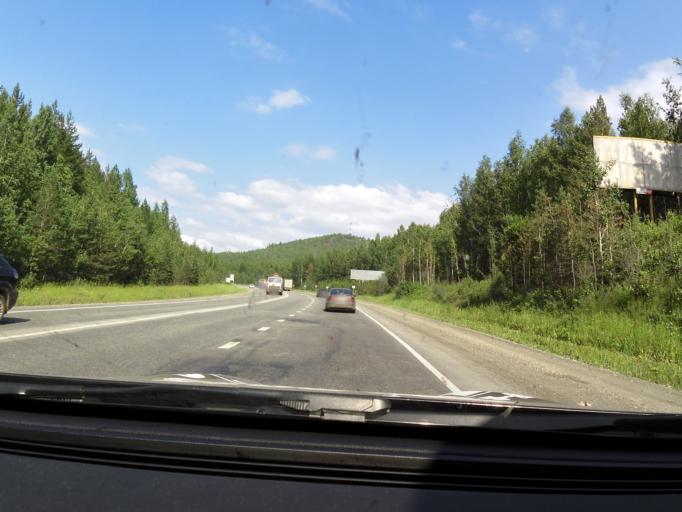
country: RU
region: Sverdlovsk
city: Revda
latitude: 56.8256
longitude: 59.9846
